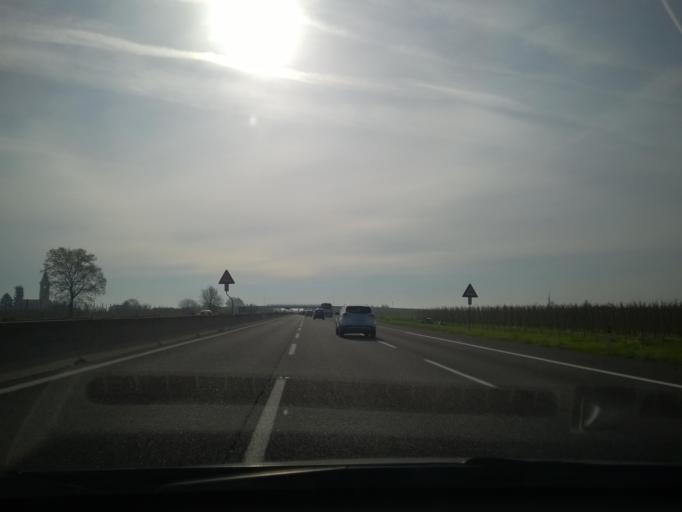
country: IT
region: Emilia-Romagna
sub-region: Provincia di Bologna
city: Mordano
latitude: 44.3602
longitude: 11.7954
